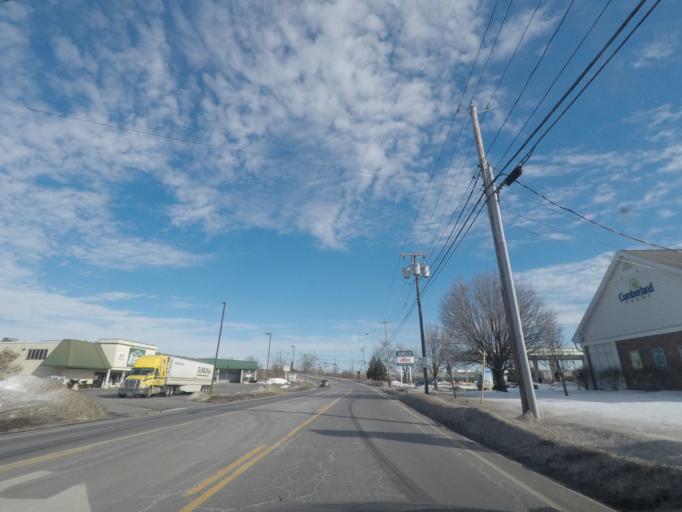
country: US
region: New York
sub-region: Schenectady County
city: Rotterdam
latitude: 42.7868
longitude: -73.9980
